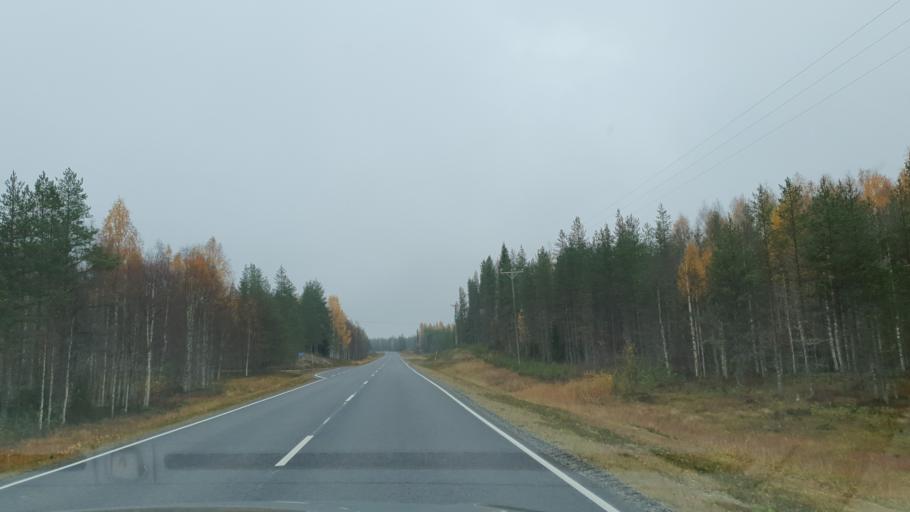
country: FI
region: Lapland
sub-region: Rovaniemi
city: Ranua
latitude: 66.1393
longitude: 26.2725
